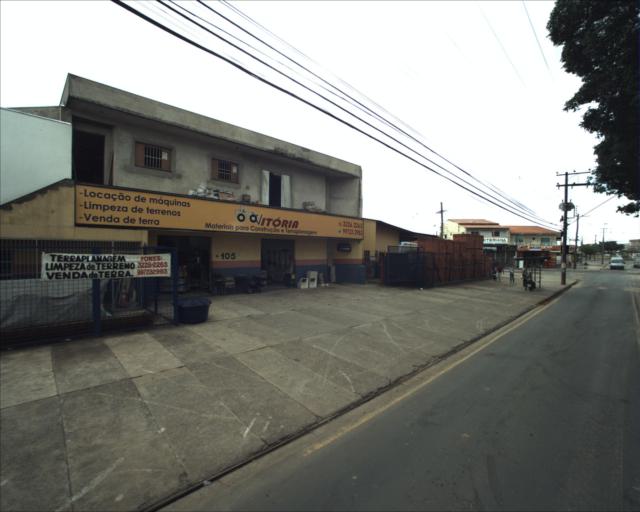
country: BR
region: Sao Paulo
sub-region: Sorocaba
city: Sorocaba
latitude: -23.4324
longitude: -47.4674
